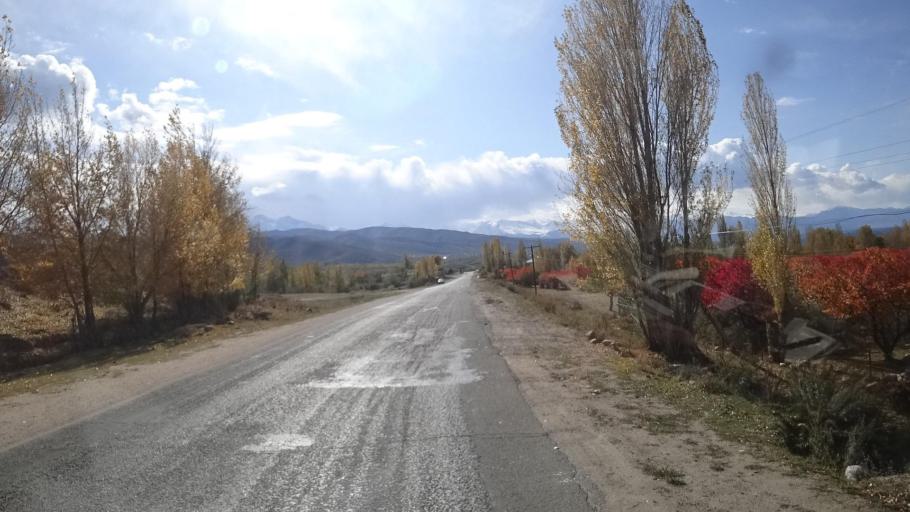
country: KG
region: Ysyk-Koel
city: Pokrovka
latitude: 42.2263
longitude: 77.7133
